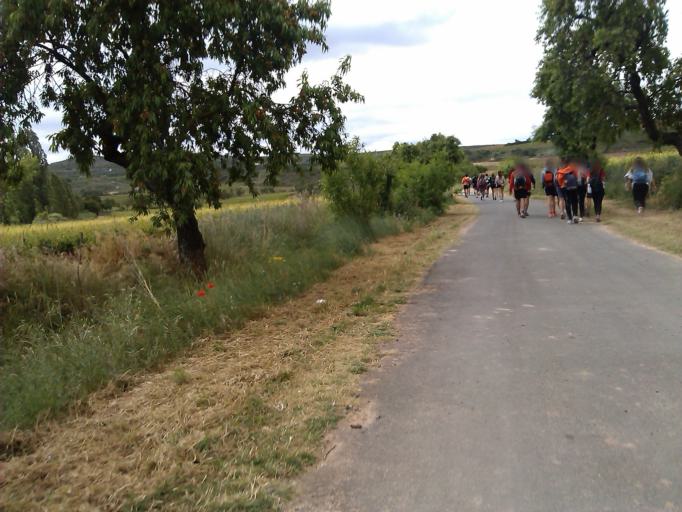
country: ES
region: La Rioja
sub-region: Provincia de La Rioja
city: Navarrete
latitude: 42.4413
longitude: -2.5148
